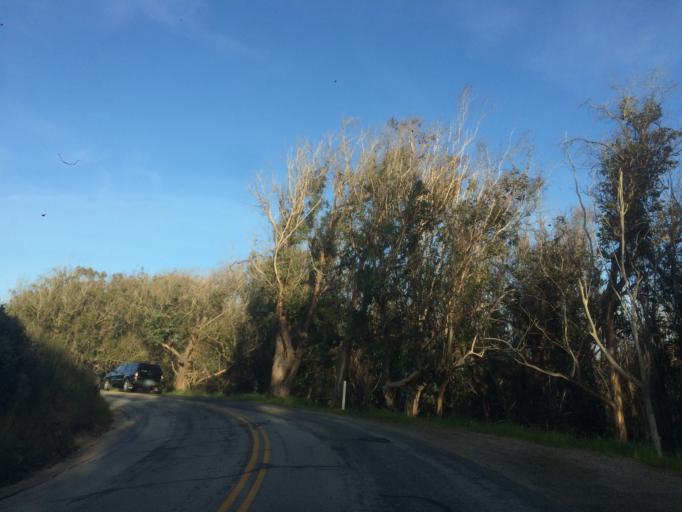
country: US
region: California
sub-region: San Luis Obispo County
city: Los Osos
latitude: 35.2975
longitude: -120.8681
